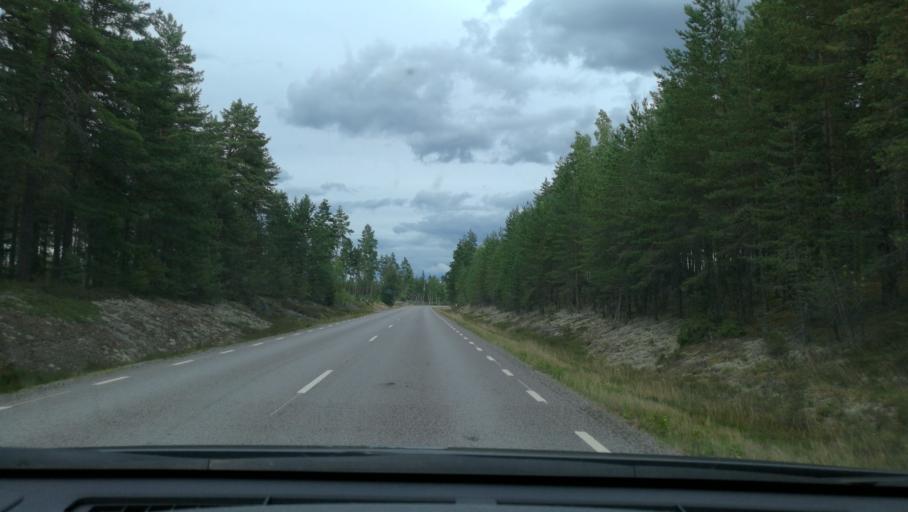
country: SE
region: OEstergoetland
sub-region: Norrkopings Kommun
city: Svartinge
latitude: 58.7360
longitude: 15.9556
